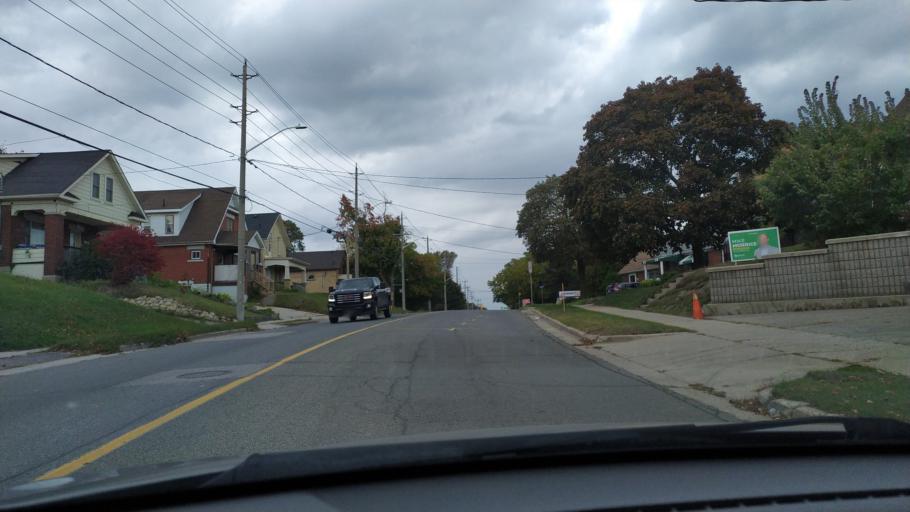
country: CA
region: Ontario
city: Waterloo
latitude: 43.4633
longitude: -80.4840
